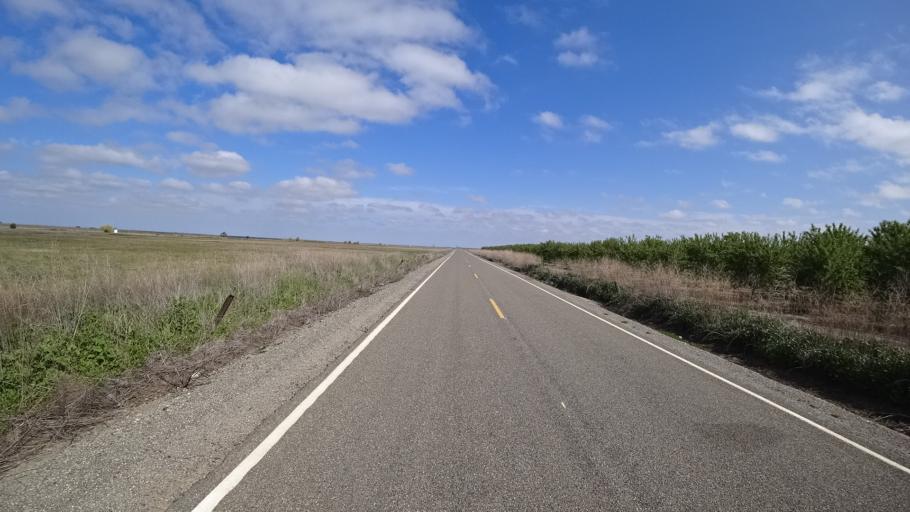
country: US
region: California
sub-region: Colusa County
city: Colusa
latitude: 39.4100
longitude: -121.9293
